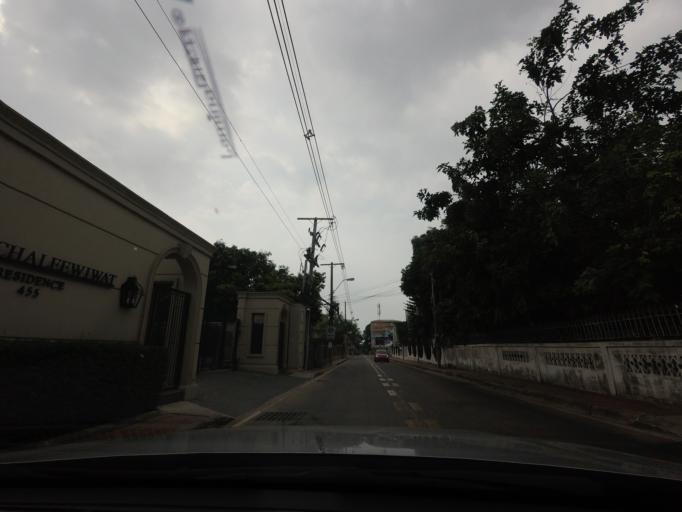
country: TH
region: Chon Buri
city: Phatthaya
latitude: 12.9634
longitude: 100.8909
